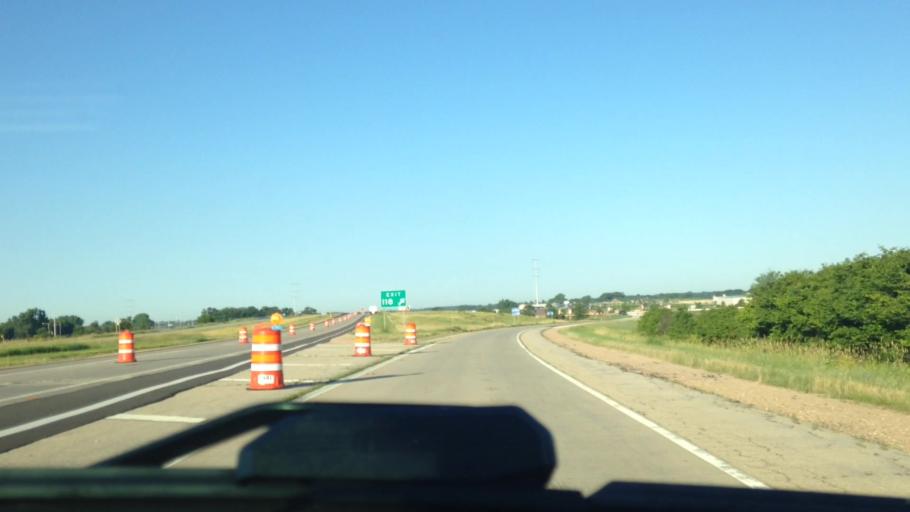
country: US
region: Wisconsin
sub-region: Columbia County
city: Columbus
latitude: 43.3511
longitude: -89.0311
